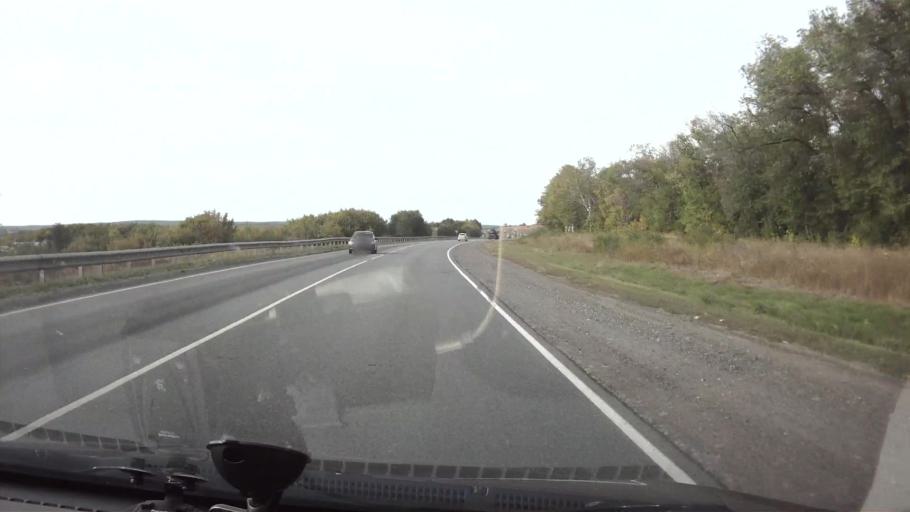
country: RU
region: Saratov
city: Tersa
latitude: 52.0890
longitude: 47.5473
